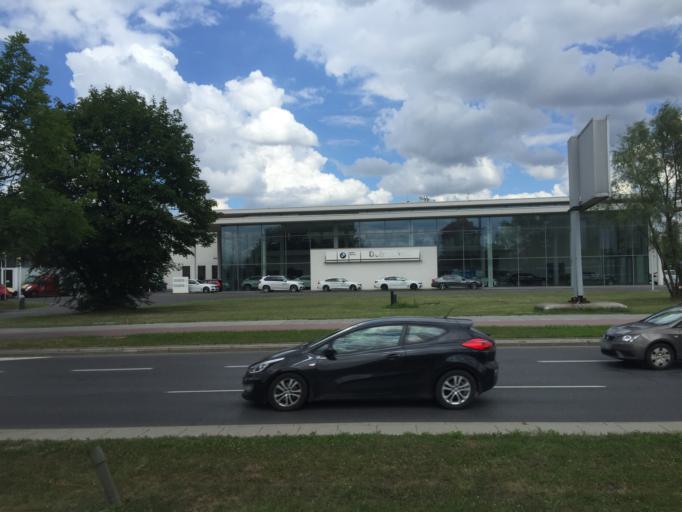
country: PL
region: Lesser Poland Voivodeship
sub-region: Krakow
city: Krakow
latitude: 50.0742
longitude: 20.0014
